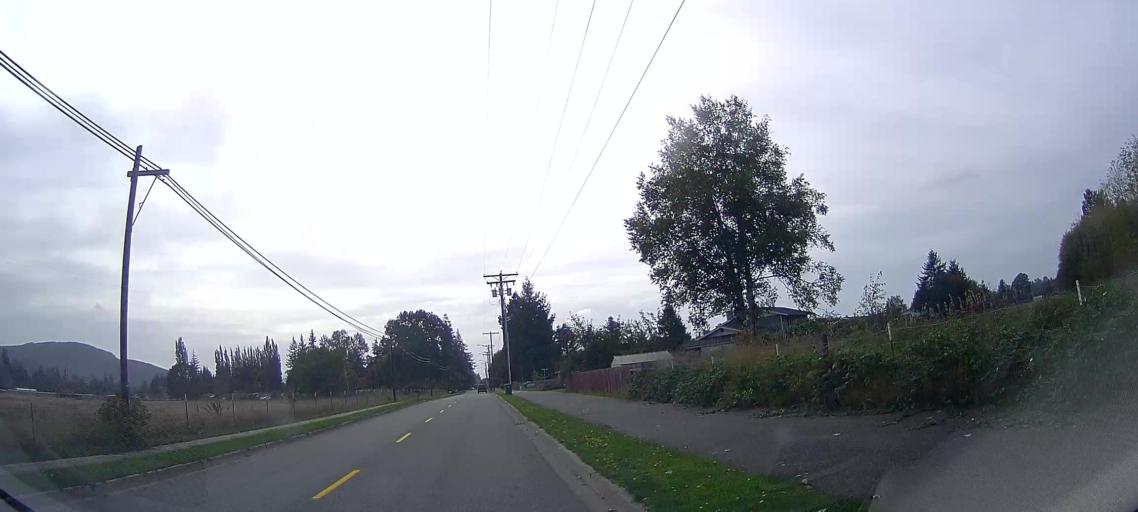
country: US
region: Washington
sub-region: Skagit County
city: Sedro-Woolley
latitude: 48.5177
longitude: -122.2172
